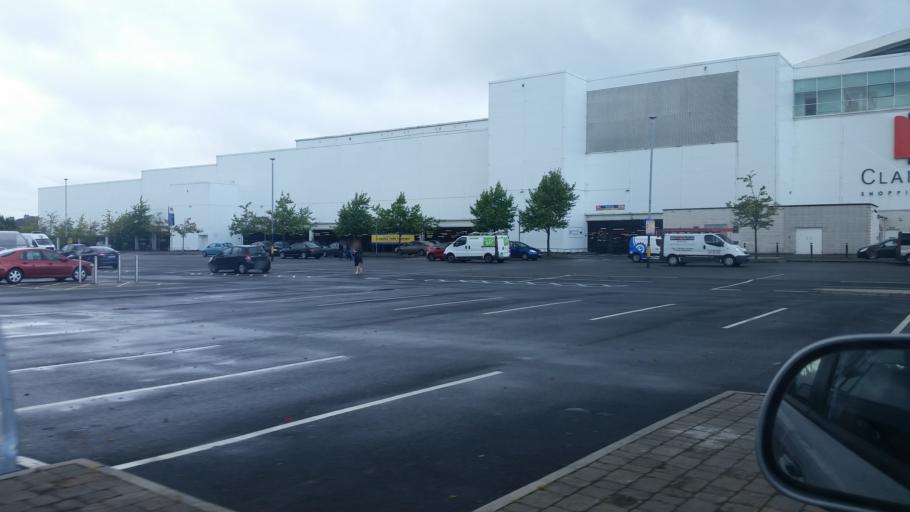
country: IE
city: Darndale
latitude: 53.4024
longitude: -6.1794
